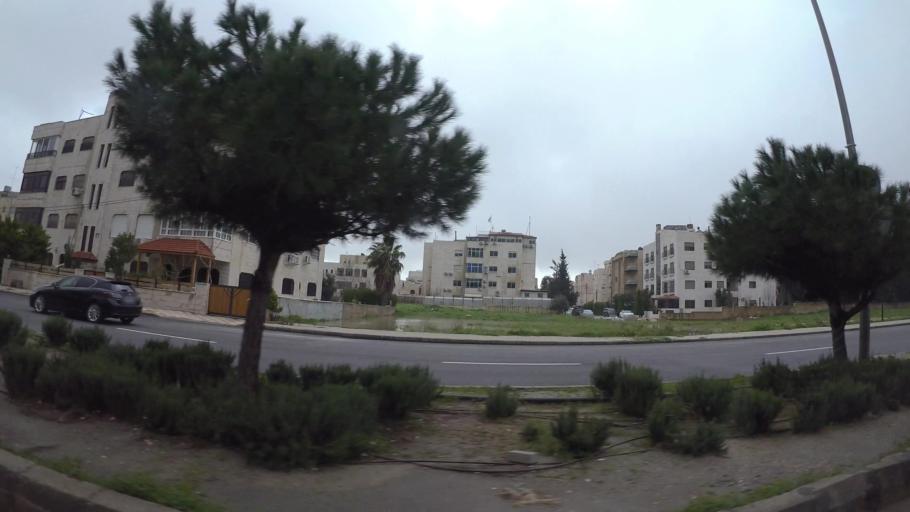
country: JO
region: Amman
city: Wadi as Sir
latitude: 31.9461
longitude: 35.8651
